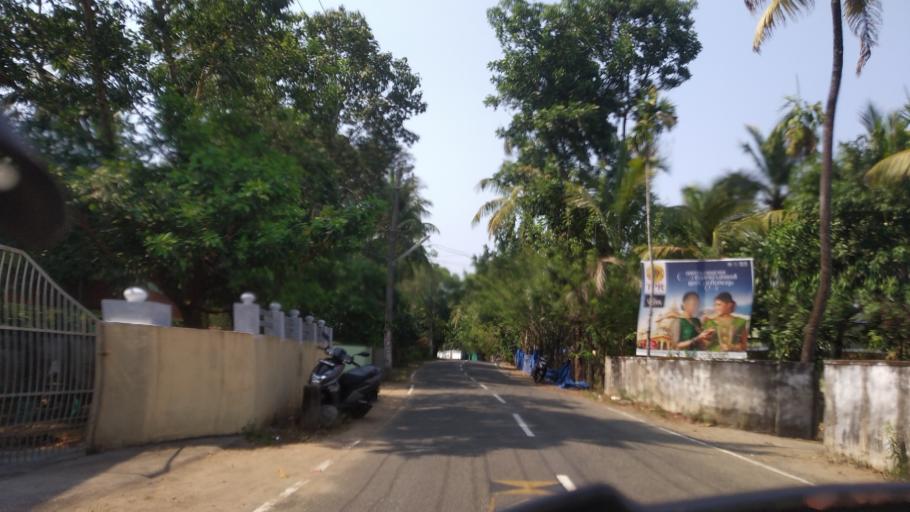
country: IN
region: Kerala
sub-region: Thrissur District
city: Thanniyam
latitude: 10.3965
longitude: 76.0946
